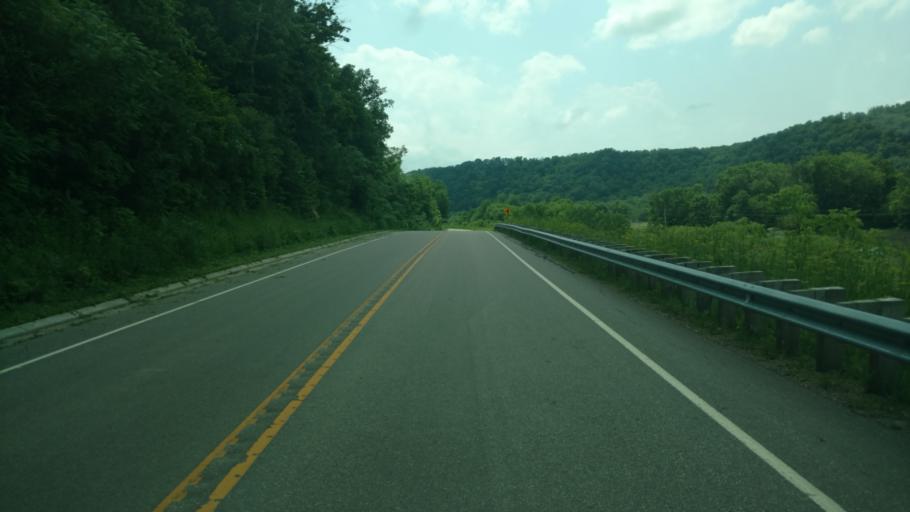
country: US
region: Wisconsin
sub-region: Vernon County
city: Viroqua
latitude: 43.4580
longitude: -90.7549
